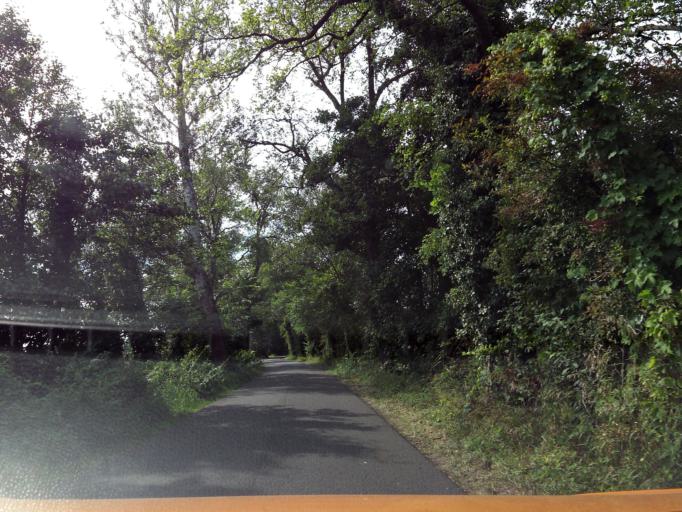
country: DE
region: Brandenburg
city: Michendorf
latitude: 52.2367
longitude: 13.1133
